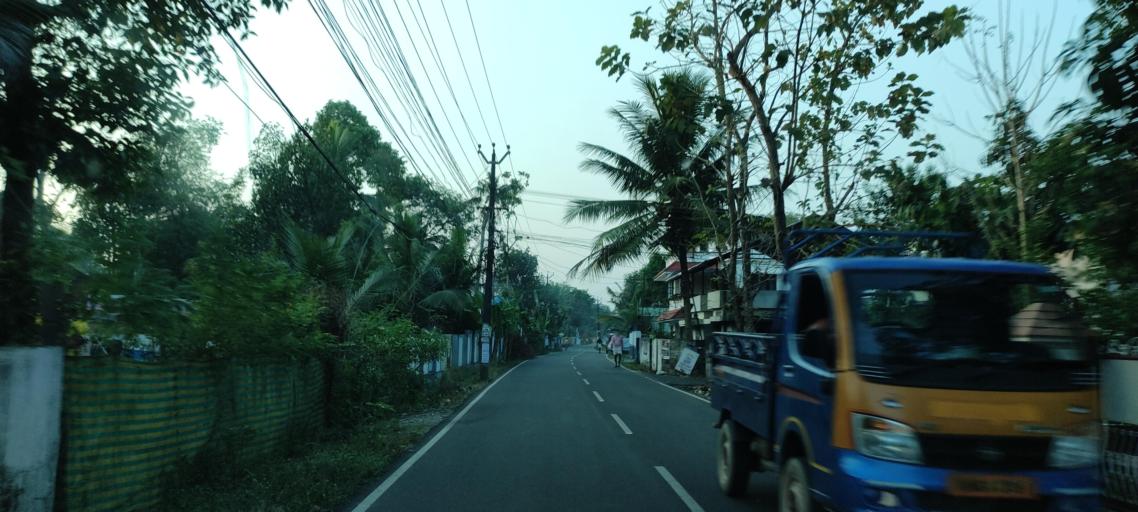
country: IN
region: Kerala
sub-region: Alappuzha
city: Alleppey
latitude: 9.4406
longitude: 76.3468
